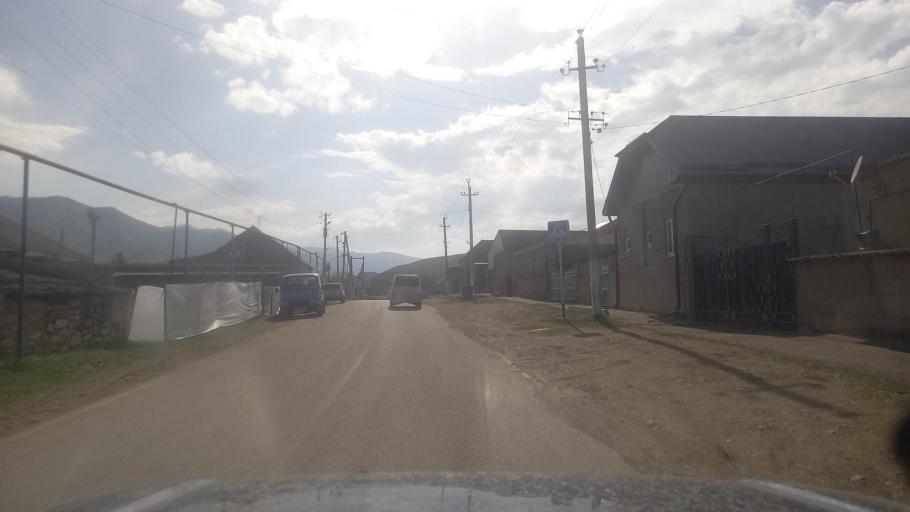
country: RU
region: Kabardino-Balkariya
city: Kamennomostskoye
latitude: 43.7293
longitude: 42.9315
